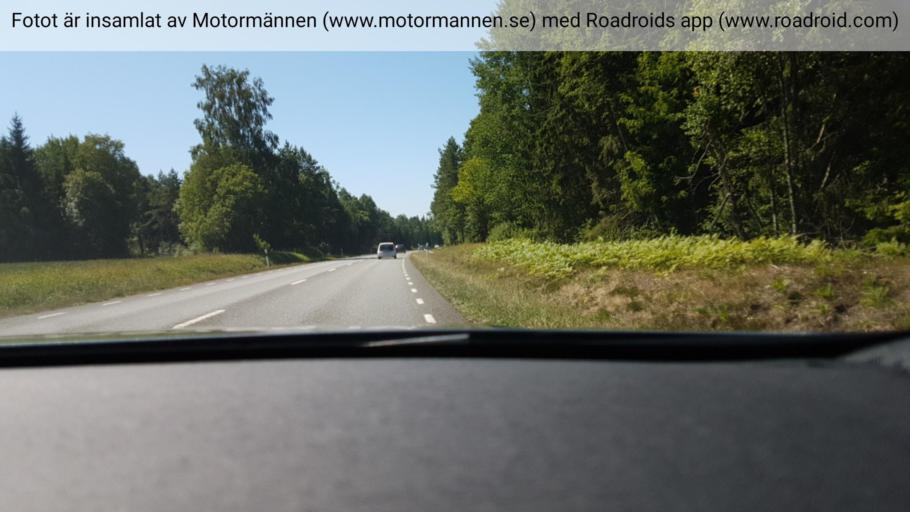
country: SE
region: Joenkoeping
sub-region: Jonkopings Kommun
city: Taberg
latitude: 57.6687
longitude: 13.8397
